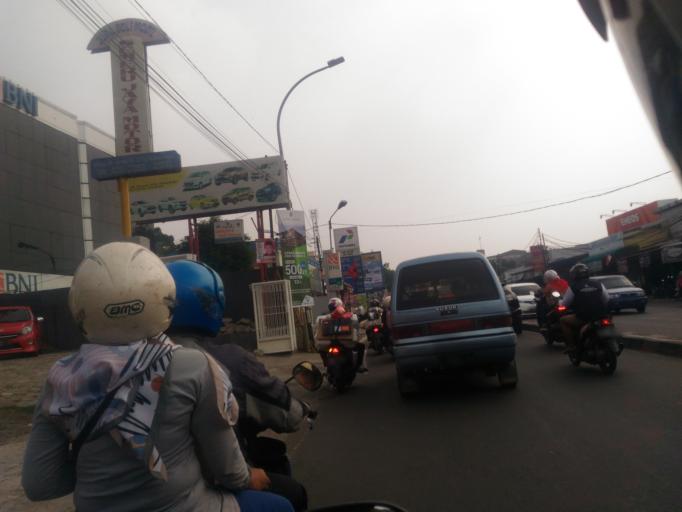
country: ID
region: West Java
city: Bogor
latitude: -6.5655
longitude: 106.8104
